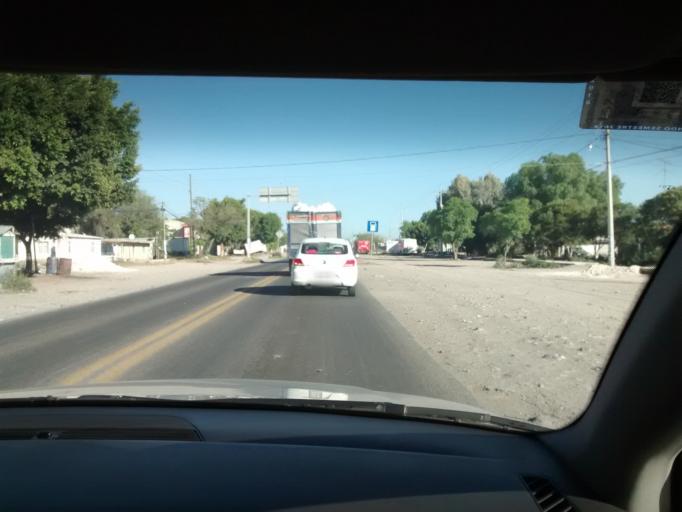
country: MX
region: Puebla
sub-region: Tehuacan
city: Magdalena Cuayucatepec
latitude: 18.5163
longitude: -97.5002
